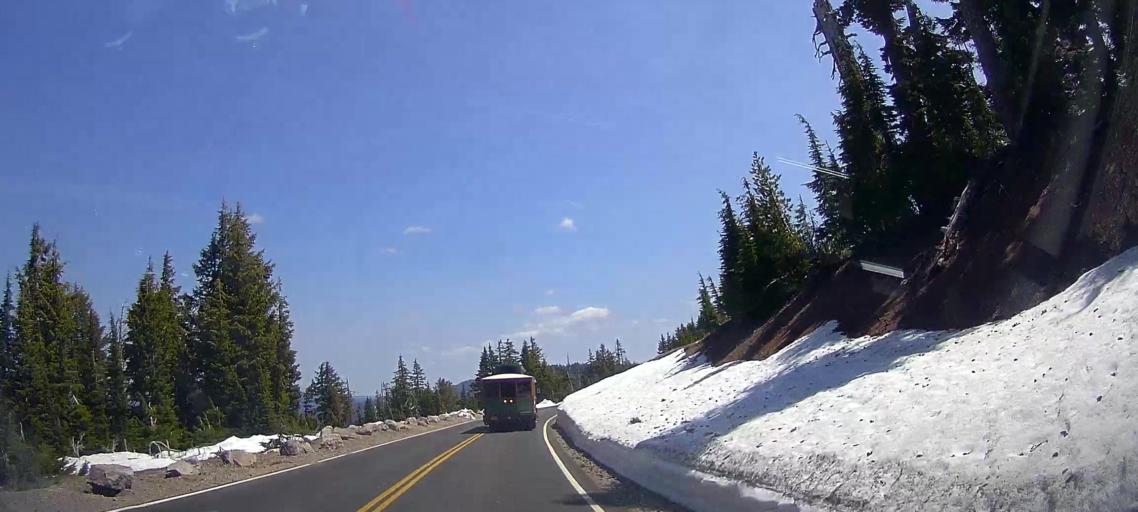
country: US
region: Oregon
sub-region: Jackson County
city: Shady Cove
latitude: 42.9790
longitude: -122.1416
